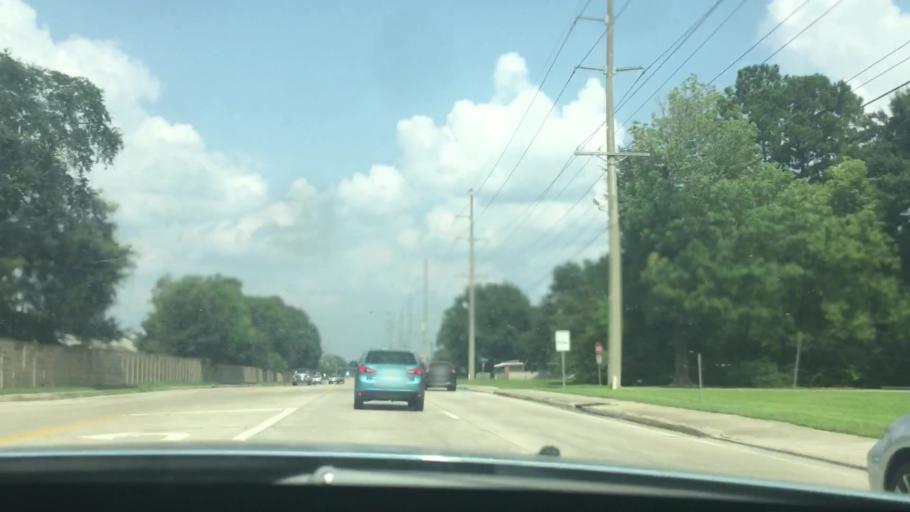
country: US
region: Louisiana
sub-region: East Baton Rouge Parish
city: Westminster
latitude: 30.4347
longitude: -91.0655
